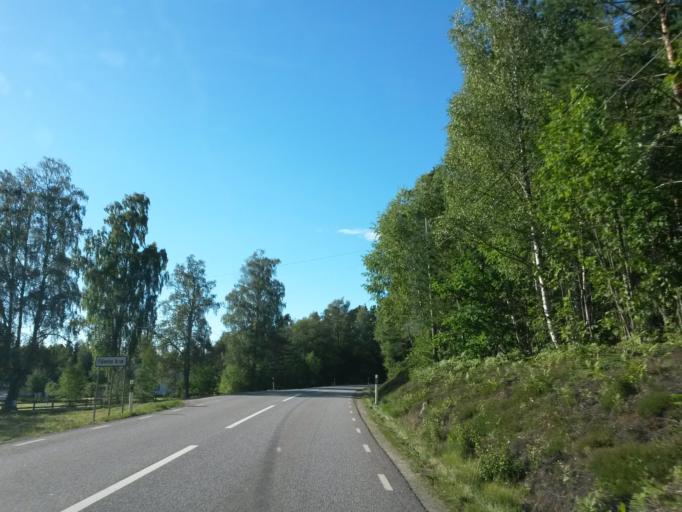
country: SE
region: Vaestra Goetaland
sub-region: Vargarda Kommun
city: Vargarda
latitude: 57.9042
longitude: 12.9081
